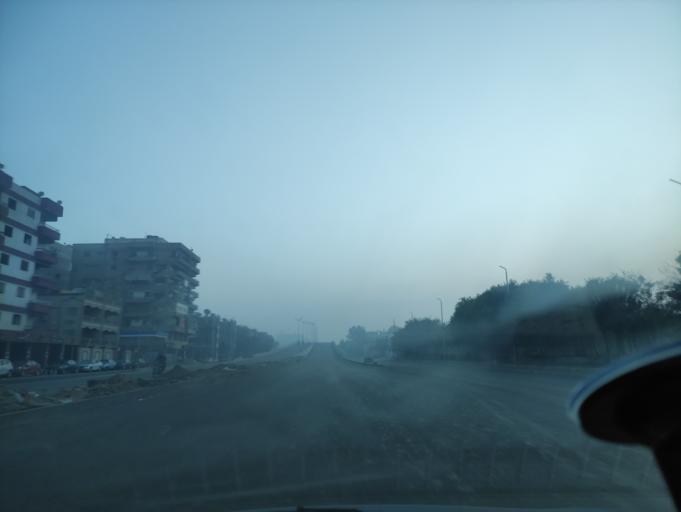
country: EG
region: Muhafazat al Qahirah
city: Cairo
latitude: 30.0461
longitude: 31.3528
